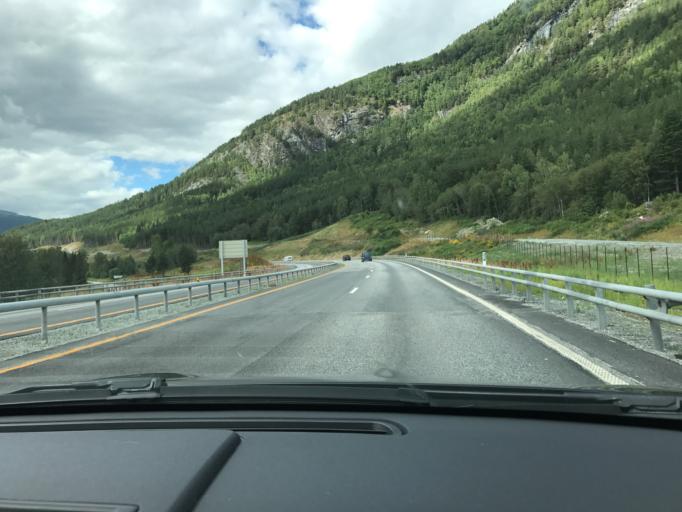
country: NO
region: Oppland
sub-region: Nord-Fron
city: Vinstra
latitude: 61.6644
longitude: 9.6468
